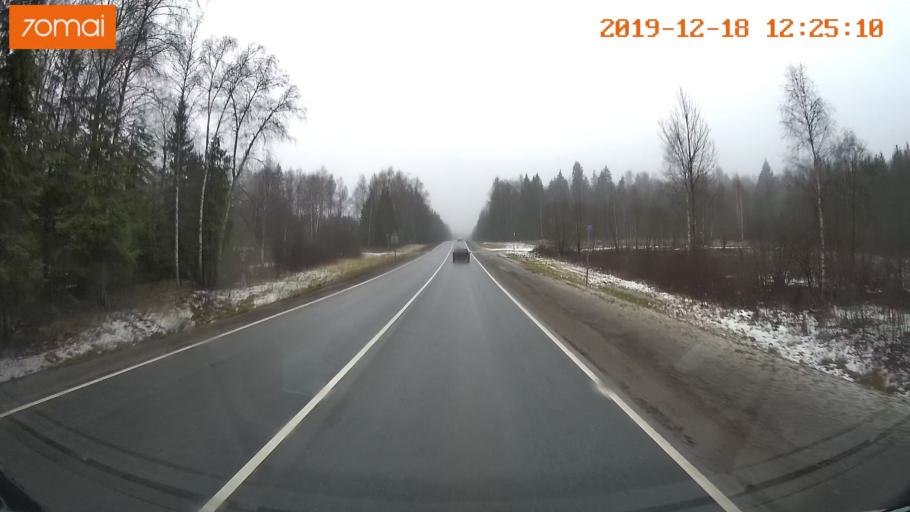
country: RU
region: Moskovskaya
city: Novopetrovskoye
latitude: 56.0343
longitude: 36.5000
